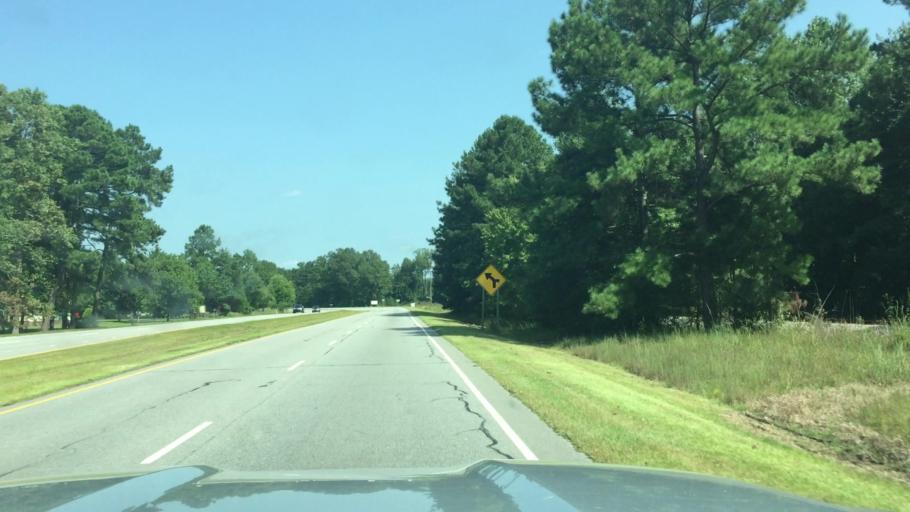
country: US
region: North Carolina
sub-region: Martin County
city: Williamston
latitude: 35.8073
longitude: -76.9445
